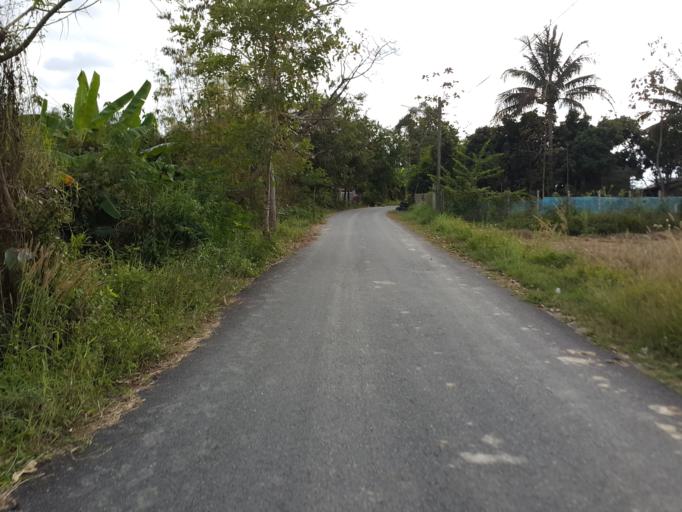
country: TH
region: Chiang Mai
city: San Sai
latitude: 18.8760
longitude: 99.1120
